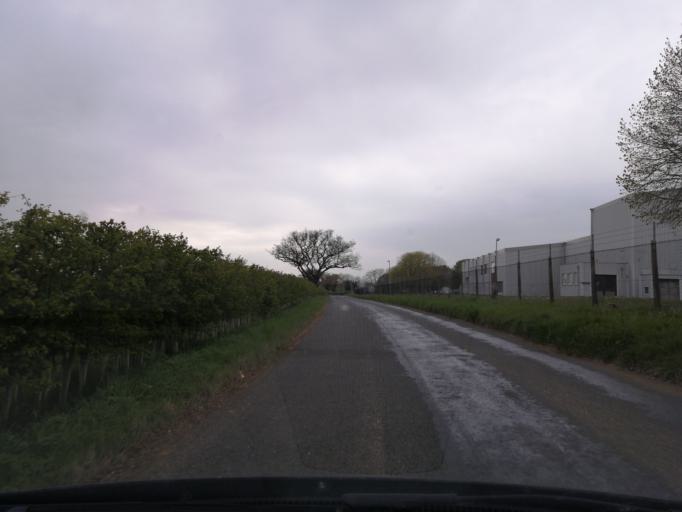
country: GB
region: England
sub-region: Peterborough
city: Wittering
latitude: 52.6105
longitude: -0.4559
